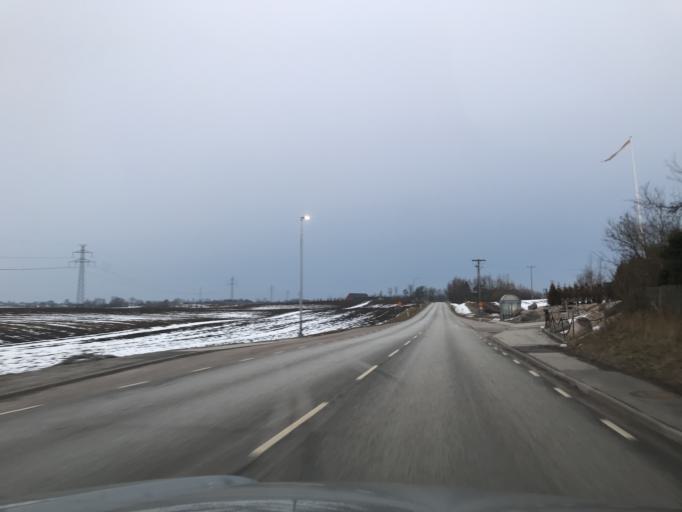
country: SE
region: Skane
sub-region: Malmo
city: Oxie
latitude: 55.5173
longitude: 13.0876
